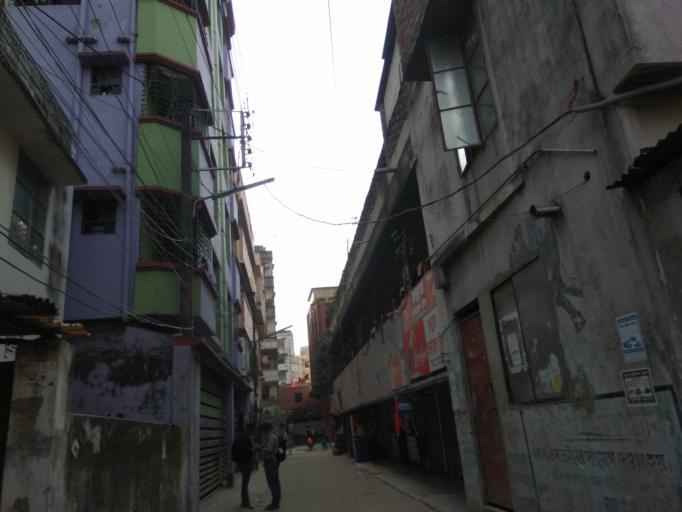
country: BD
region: Dhaka
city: Azimpur
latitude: 23.7730
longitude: 90.3576
